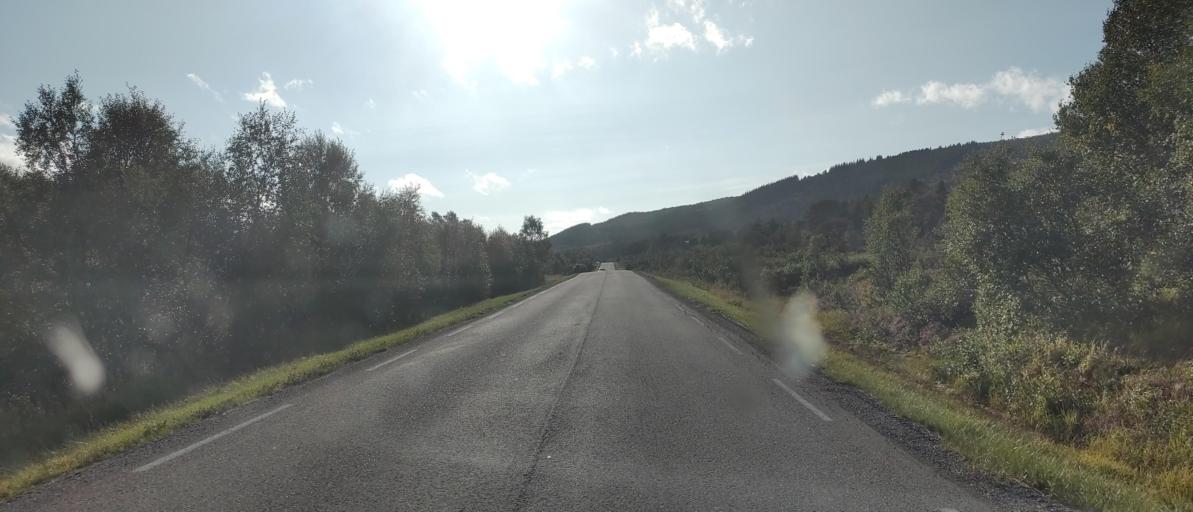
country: NO
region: Nordland
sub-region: Sortland
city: Sortland
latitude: 68.7970
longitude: 15.5293
